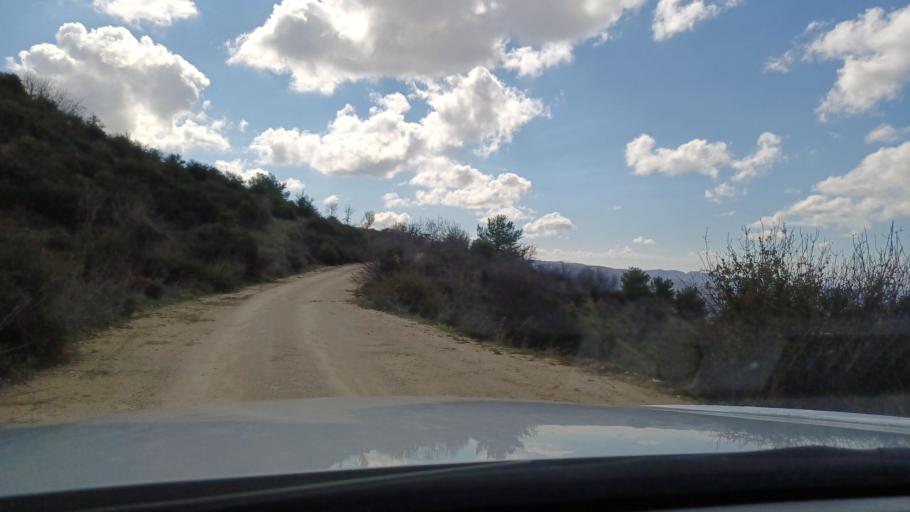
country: CY
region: Limassol
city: Pachna
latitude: 34.8351
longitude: 32.7642
